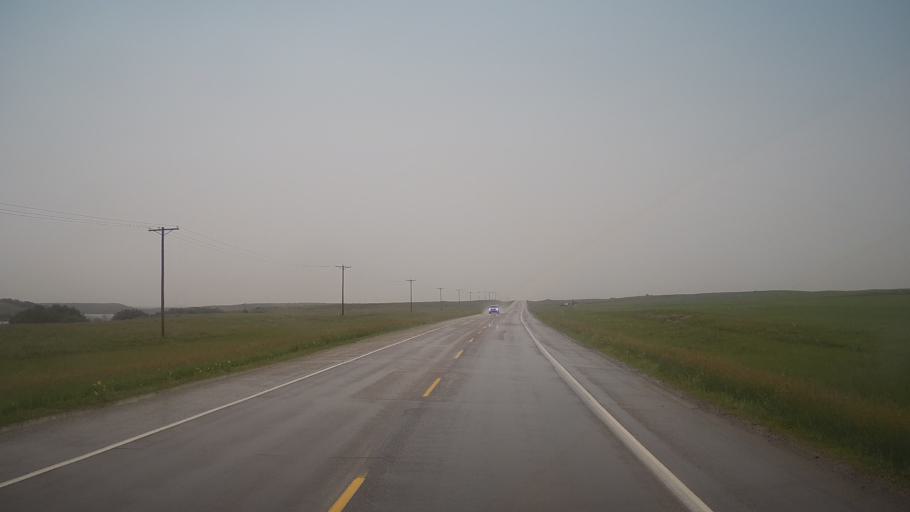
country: CA
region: Saskatchewan
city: Biggar
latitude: 52.0747
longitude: -108.0201
